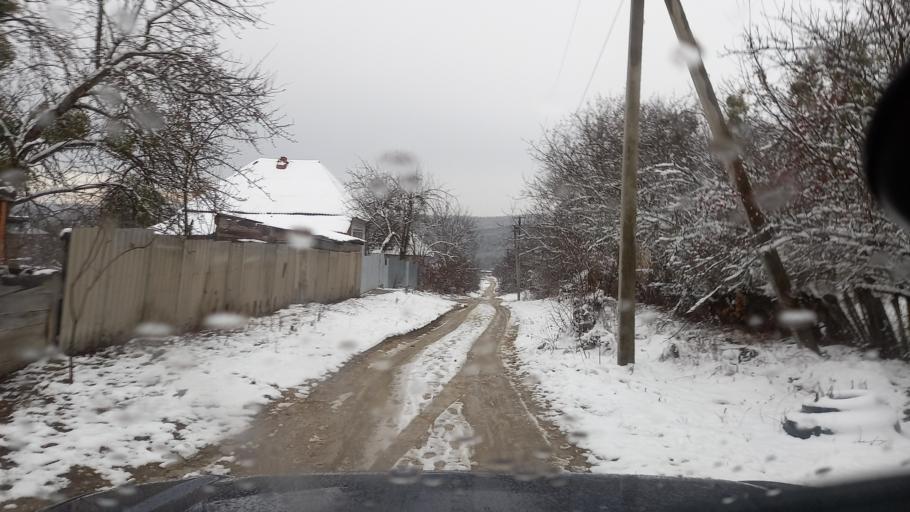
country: RU
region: Adygeya
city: Abadzekhskaya
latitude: 44.3501
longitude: 40.4074
